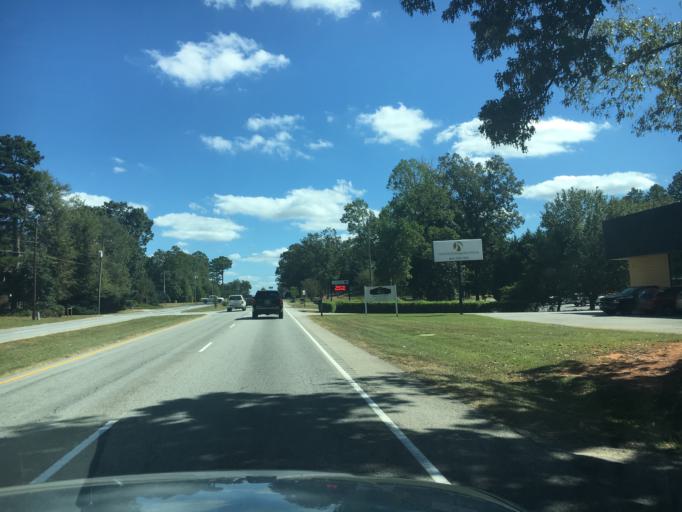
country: US
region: South Carolina
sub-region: Spartanburg County
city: Fairforest
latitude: 34.9365
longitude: -82.0167
